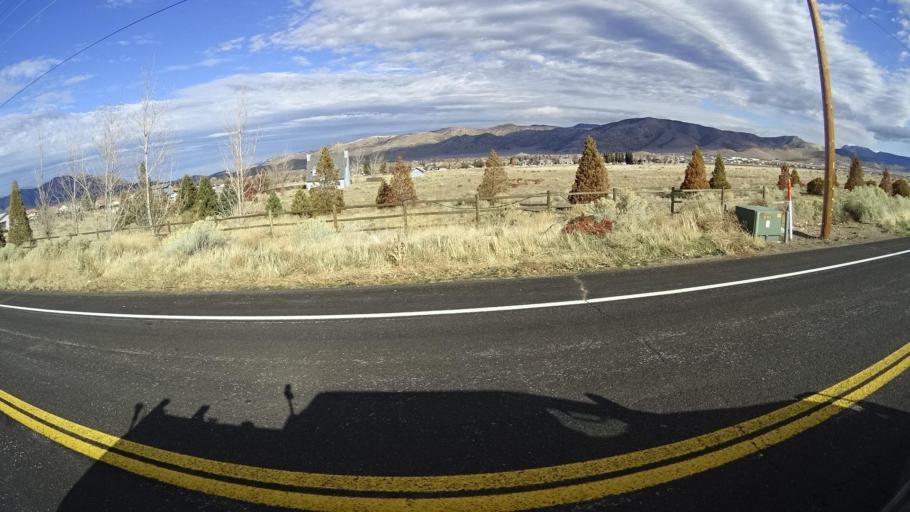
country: US
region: California
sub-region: Kern County
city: Tehachapi
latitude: 35.1094
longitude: -118.4430
